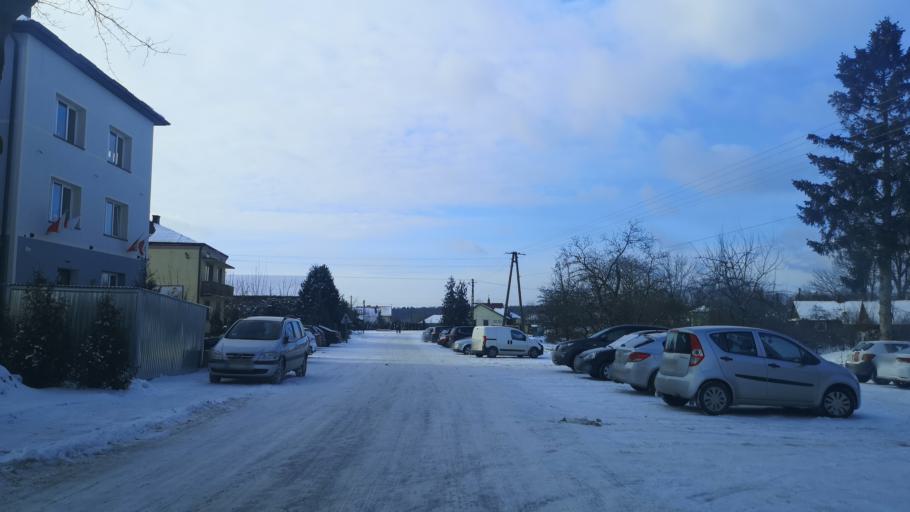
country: PL
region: Subcarpathian Voivodeship
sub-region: Powiat przeworski
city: Adamowka
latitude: 50.2589
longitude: 22.6944
